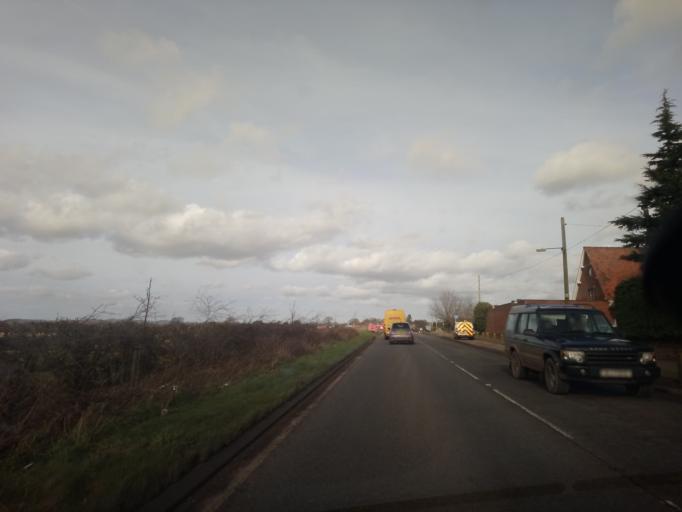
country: GB
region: England
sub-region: Telford and Wrekin
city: Eyton upon the Weald Moors
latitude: 52.7634
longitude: -2.5466
